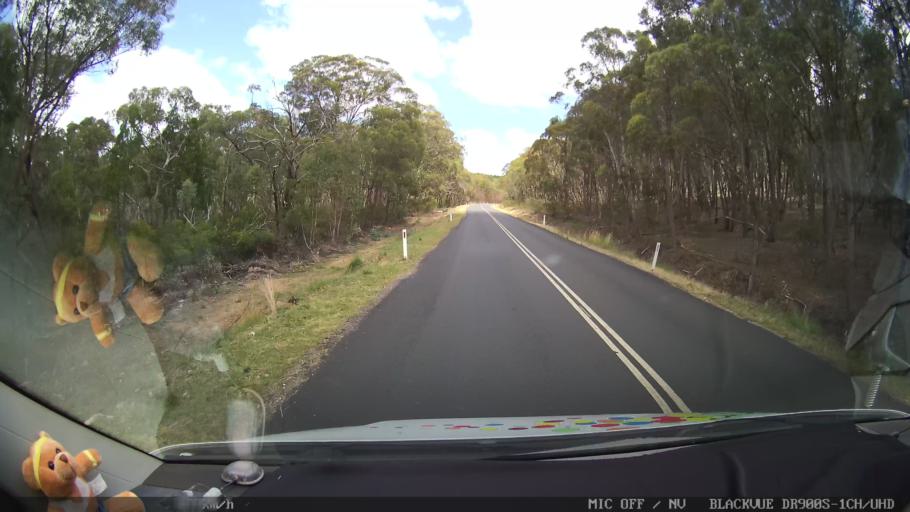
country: AU
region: New South Wales
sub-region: Glen Innes Severn
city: Glen Innes
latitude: -29.4574
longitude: 151.6075
